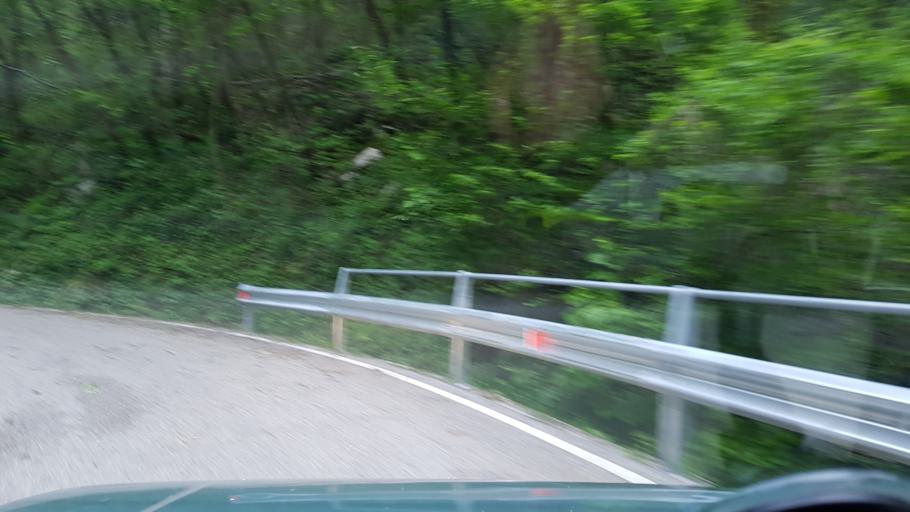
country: IT
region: Friuli Venezia Giulia
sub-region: Provincia di Udine
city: Faedis
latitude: 46.1715
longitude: 13.3582
